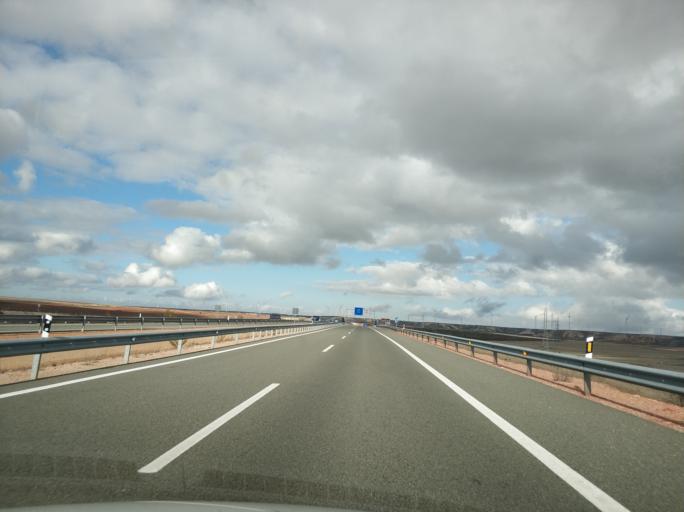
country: ES
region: Castille and Leon
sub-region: Provincia de Soria
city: Alcubilla de las Penas
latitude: 41.2527
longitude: -2.4737
